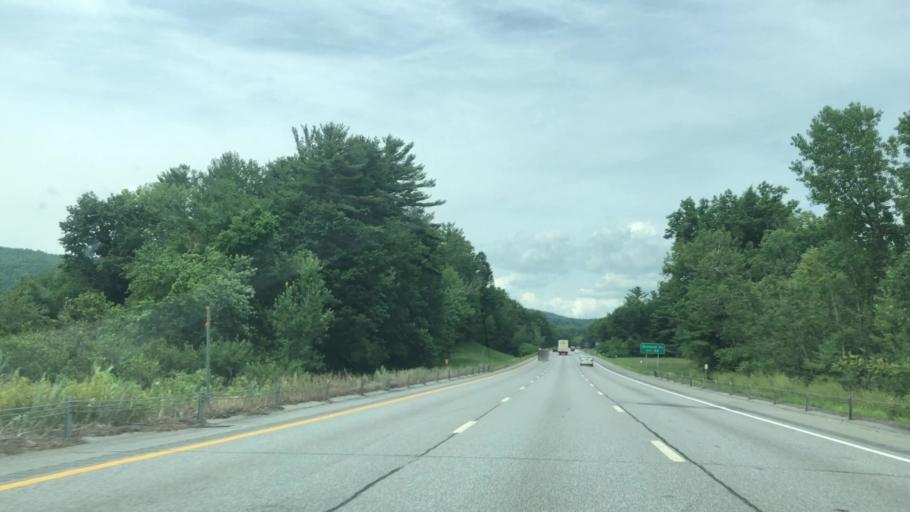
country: US
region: New York
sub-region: Warren County
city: Glens Falls North
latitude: 43.3496
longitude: -73.6963
